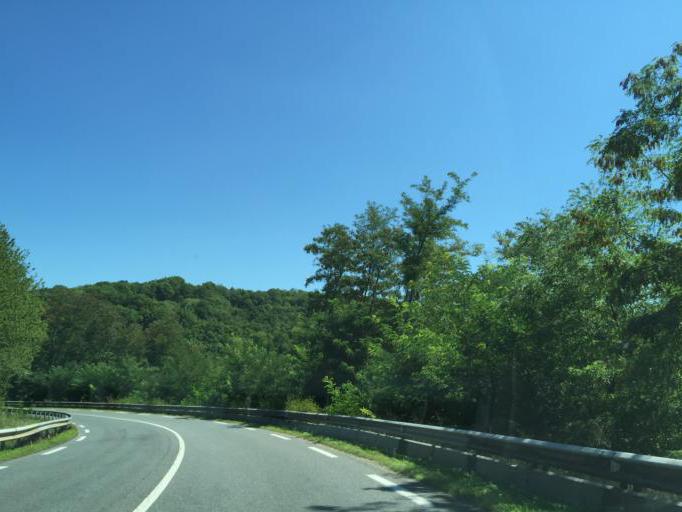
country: FR
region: Midi-Pyrenees
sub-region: Departement de l'Aveyron
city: Espalion
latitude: 44.5134
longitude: 2.7531
